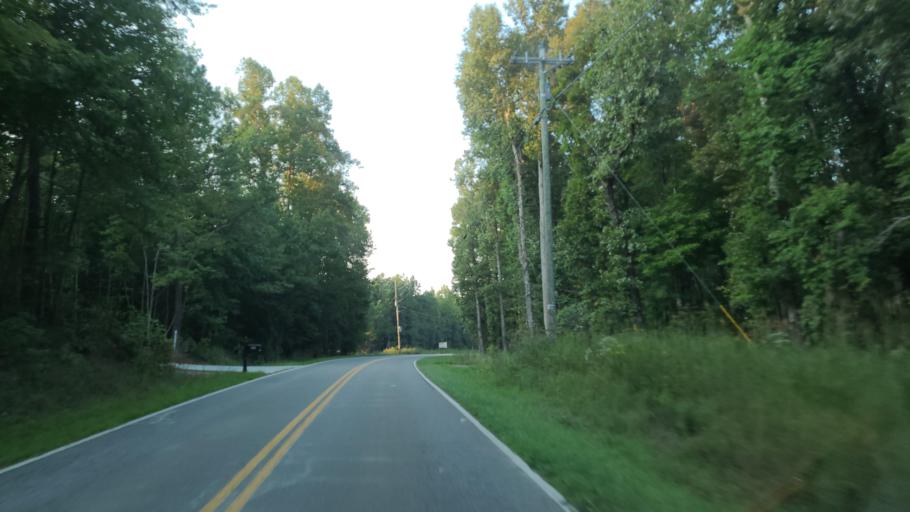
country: US
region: Georgia
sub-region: Pickens County
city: Jasper
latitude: 34.4710
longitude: -84.5550
